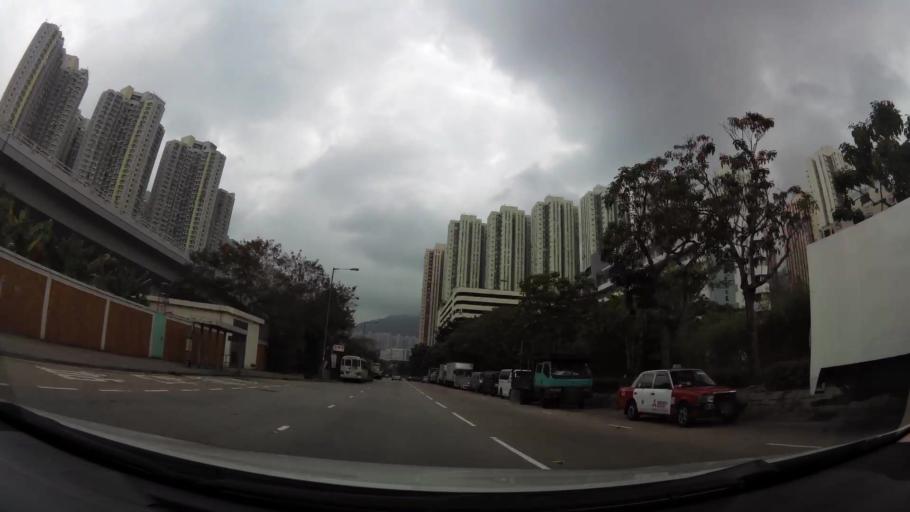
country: HK
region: Kowloon City
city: Kowloon
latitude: 22.3280
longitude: 114.2057
